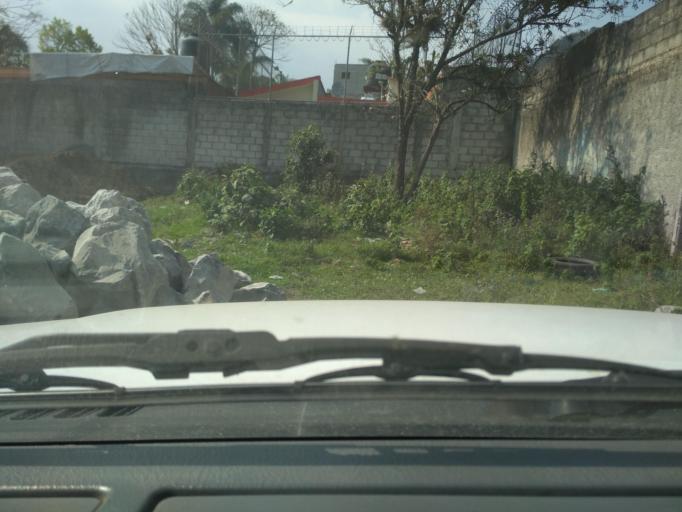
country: MX
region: Veracruz
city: Orizaba
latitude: 18.8704
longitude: -97.0945
